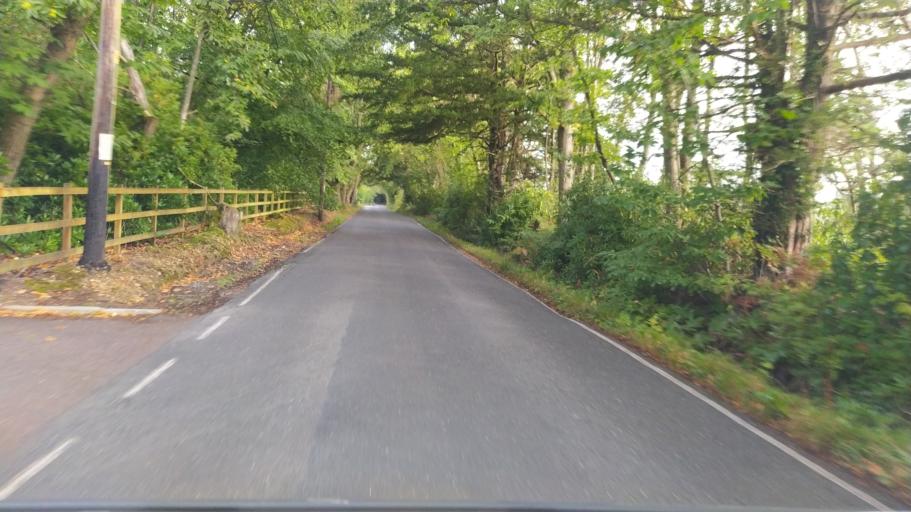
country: GB
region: England
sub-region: Hampshire
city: Romsey
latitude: 50.9818
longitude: -1.5311
